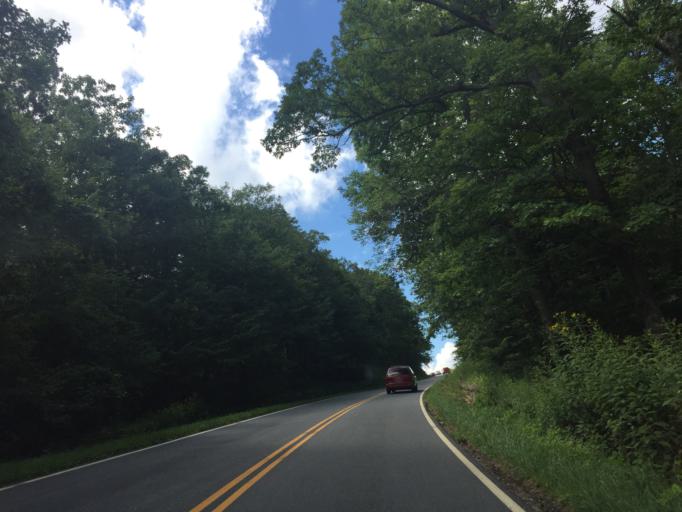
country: US
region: Virginia
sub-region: Rappahannock County
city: Washington
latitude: 38.7624
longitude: -78.2425
